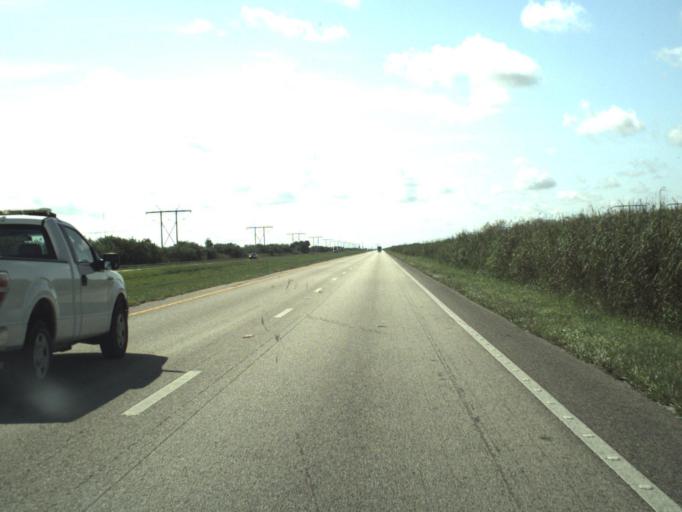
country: US
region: Florida
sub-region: Broward County
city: Weston
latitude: 26.2734
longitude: -80.4906
